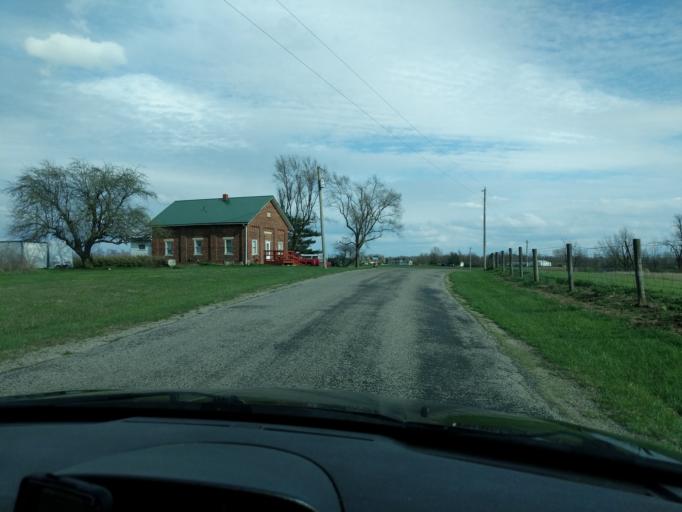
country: US
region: Ohio
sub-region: Champaign County
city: North Lewisburg
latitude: 40.1942
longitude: -83.6527
